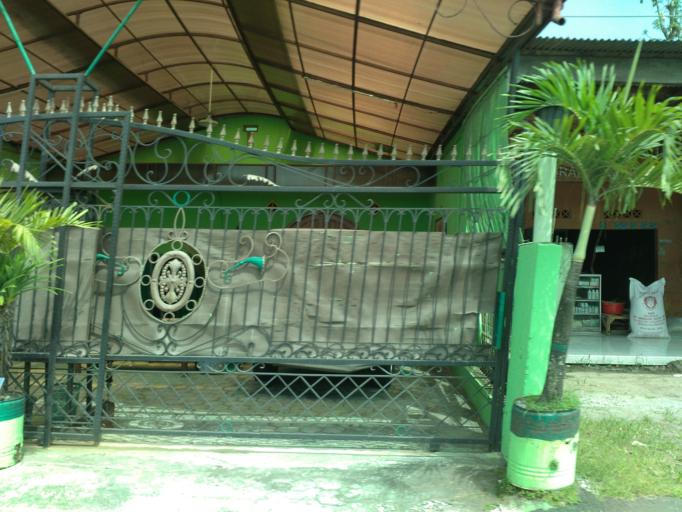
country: ID
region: Central Java
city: Candi Prambanan
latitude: -7.7432
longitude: 110.5295
